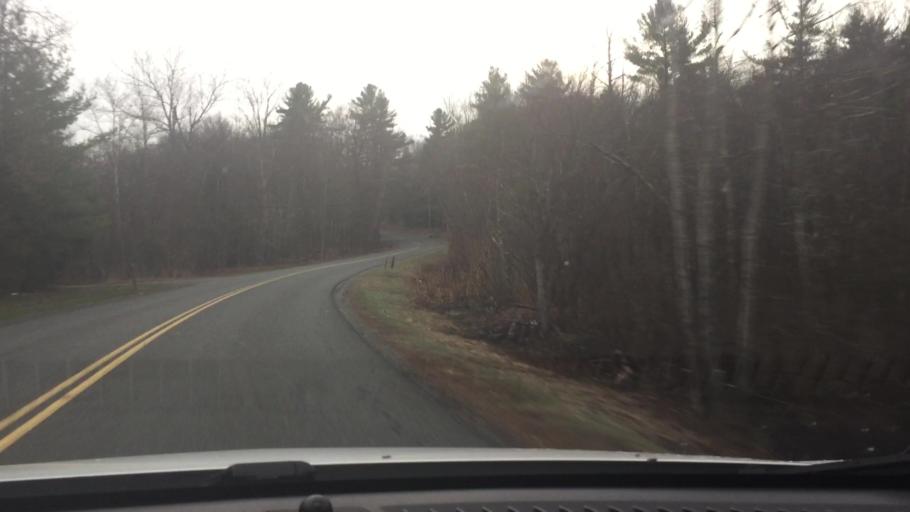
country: US
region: Massachusetts
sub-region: Berkshire County
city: Otis
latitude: 42.1911
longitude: -73.0327
